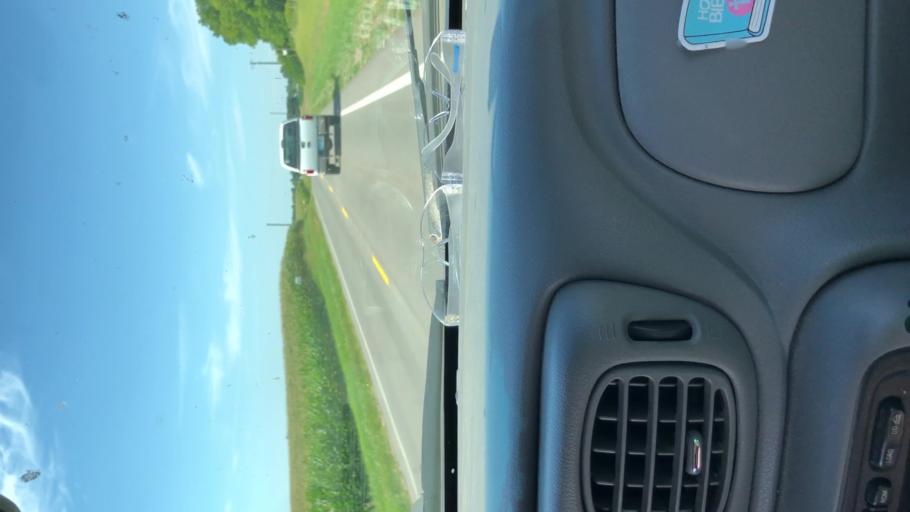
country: US
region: Ohio
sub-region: Champaign County
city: Urbana
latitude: 40.0799
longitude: -83.7343
